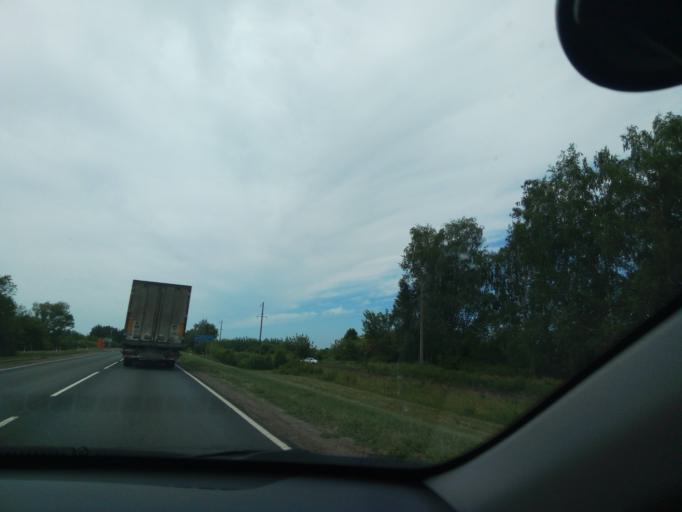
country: RU
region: Tambov
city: Selezni
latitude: 52.6479
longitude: 41.0090
